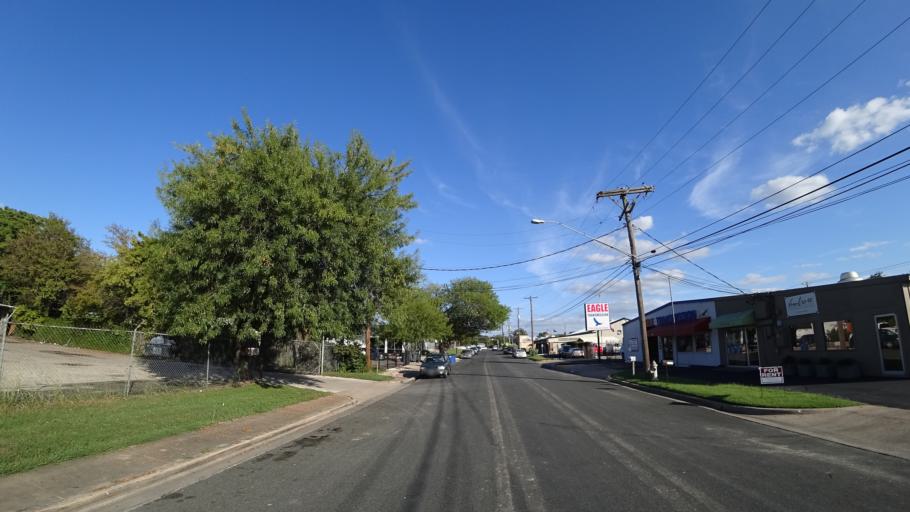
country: US
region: Texas
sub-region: Williamson County
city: Jollyville
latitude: 30.3640
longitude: -97.7307
